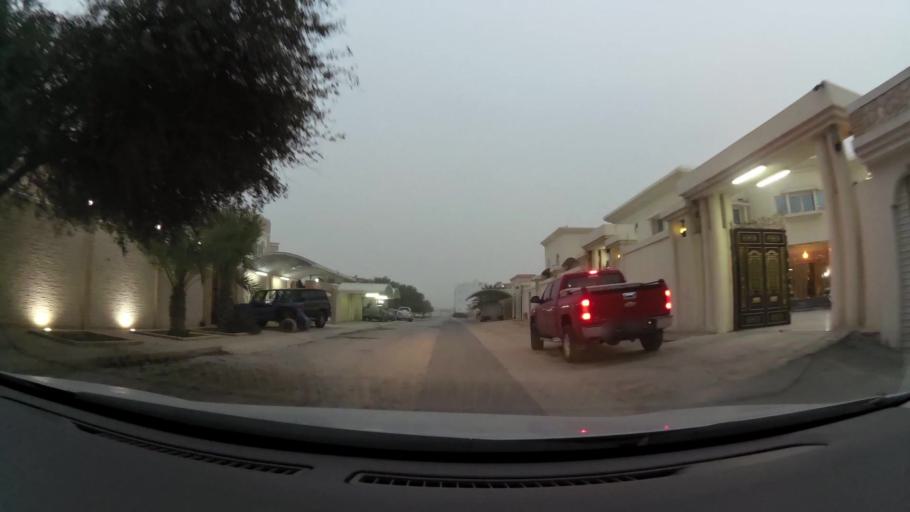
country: QA
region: Baladiyat ad Dawhah
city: Doha
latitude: 25.2297
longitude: 51.4933
